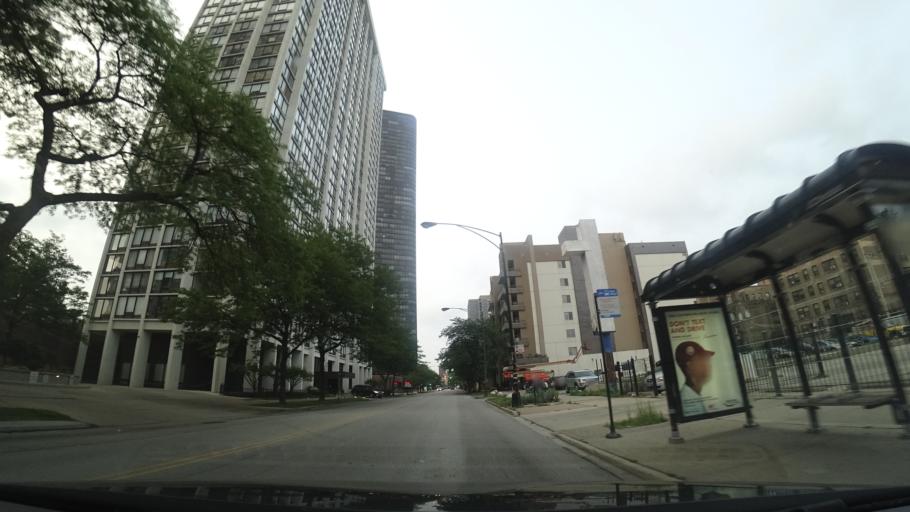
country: US
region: Illinois
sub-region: Cook County
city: Evanston
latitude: 41.9817
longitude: -87.6552
